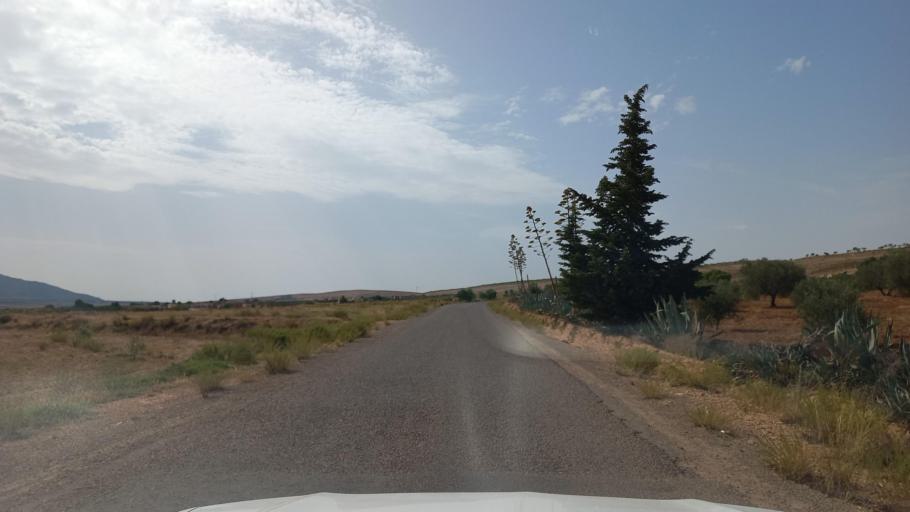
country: TN
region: Al Qasrayn
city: Kasserine
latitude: 35.3661
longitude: 8.8743
